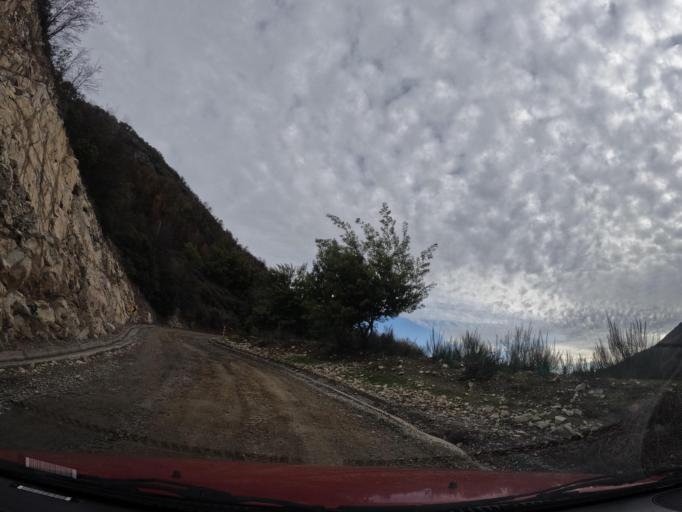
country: CL
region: Maule
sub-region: Provincia de Linares
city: Colbun
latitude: -35.8566
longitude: -71.1887
